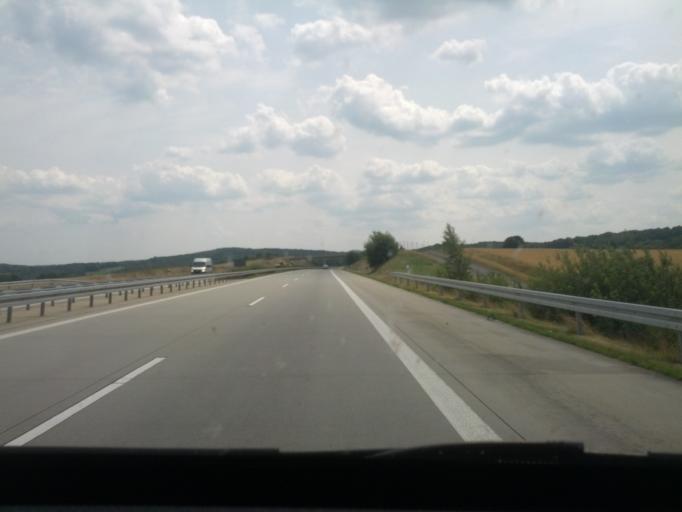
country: DE
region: Saxony
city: Liebstadt
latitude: 50.8549
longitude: 13.8768
